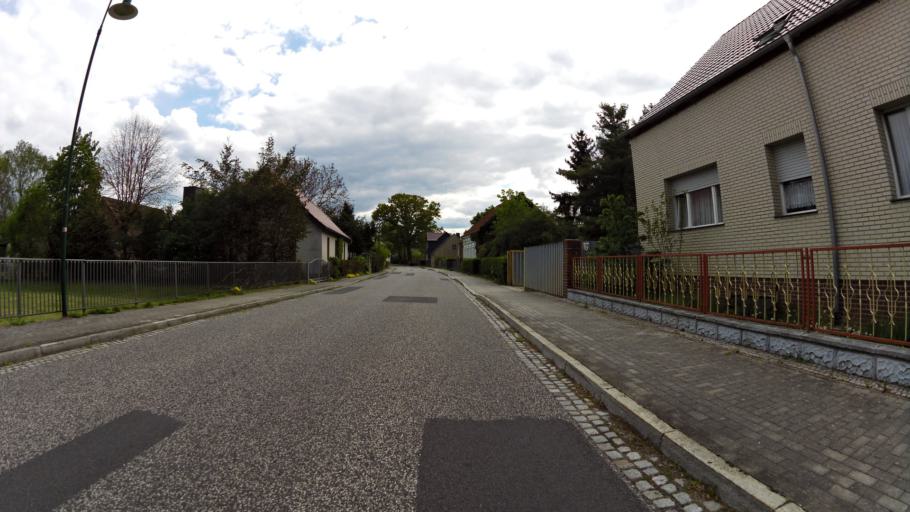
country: DE
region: Brandenburg
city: Rauen
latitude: 52.3320
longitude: 13.9519
